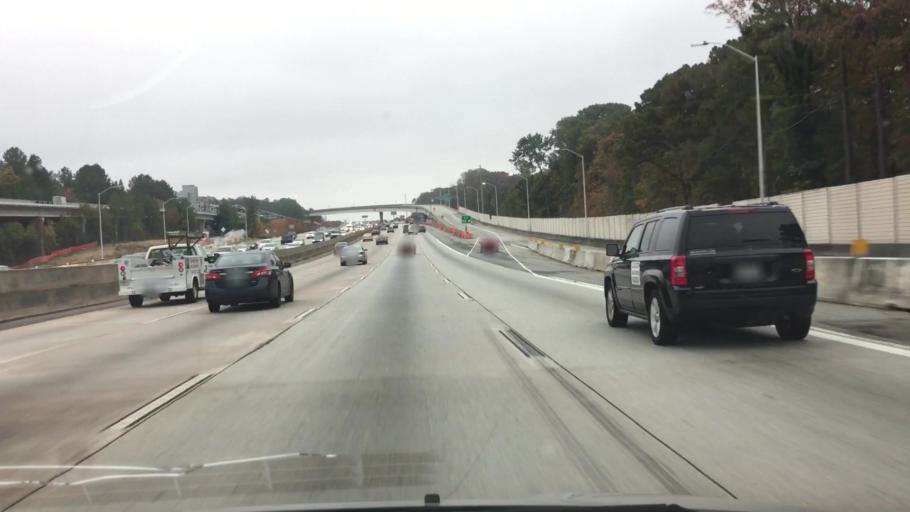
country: US
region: Georgia
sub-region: DeKalb County
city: Dunwoody
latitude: 33.9497
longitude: -84.3580
